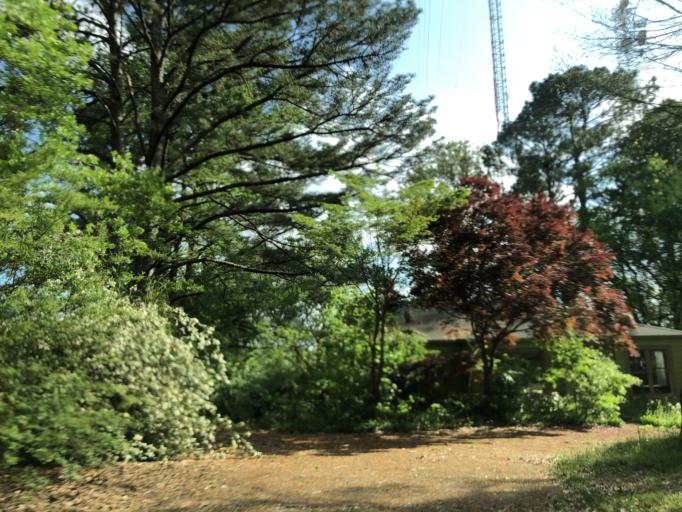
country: US
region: Georgia
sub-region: DeKalb County
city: North Druid Hills
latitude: 33.8084
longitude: -84.3401
